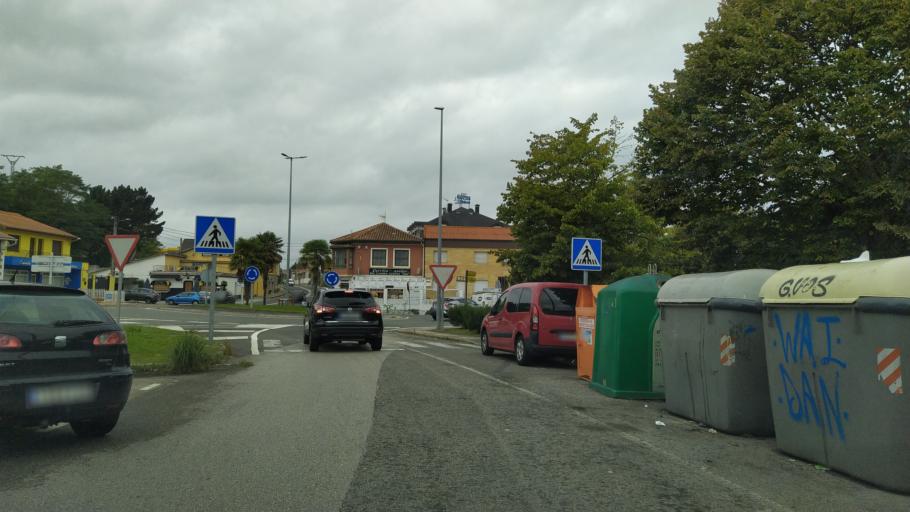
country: ES
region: Cantabria
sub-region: Provincia de Cantabria
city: Santa Cruz de Bezana
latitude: 43.4378
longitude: -3.8985
